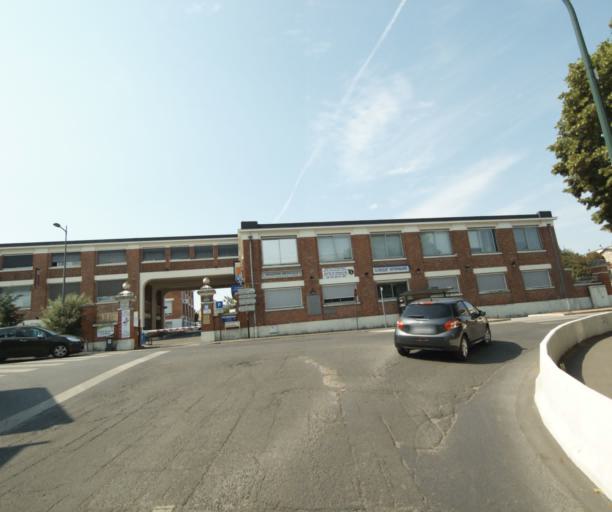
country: FR
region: Ile-de-France
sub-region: Departement des Yvelines
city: Conflans-Sainte-Honorine
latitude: 48.9989
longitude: 2.1056
